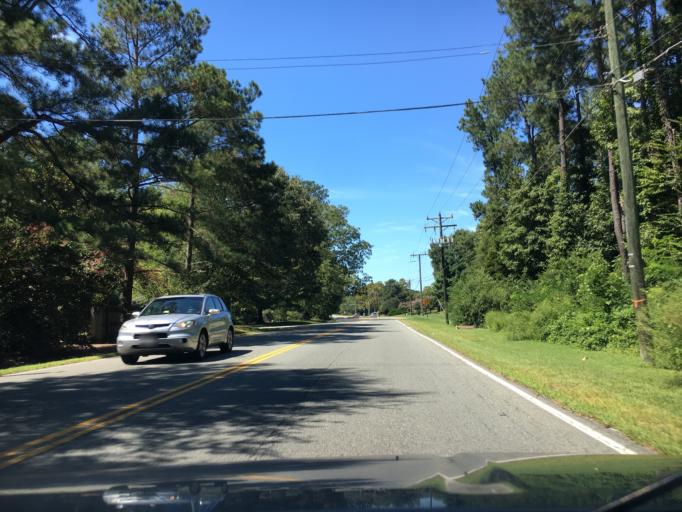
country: US
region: Virginia
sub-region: Henrico County
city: Tuckahoe
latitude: 37.5982
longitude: -77.5429
